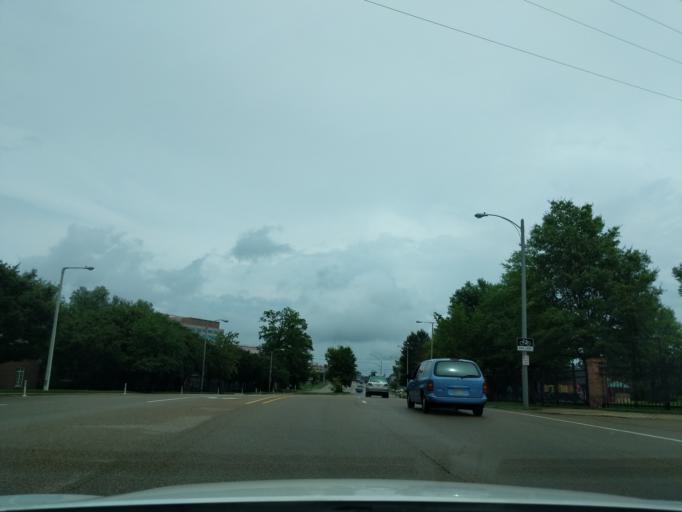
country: US
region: Tennessee
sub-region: Shelby County
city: Memphis
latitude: 35.1492
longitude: -90.0431
